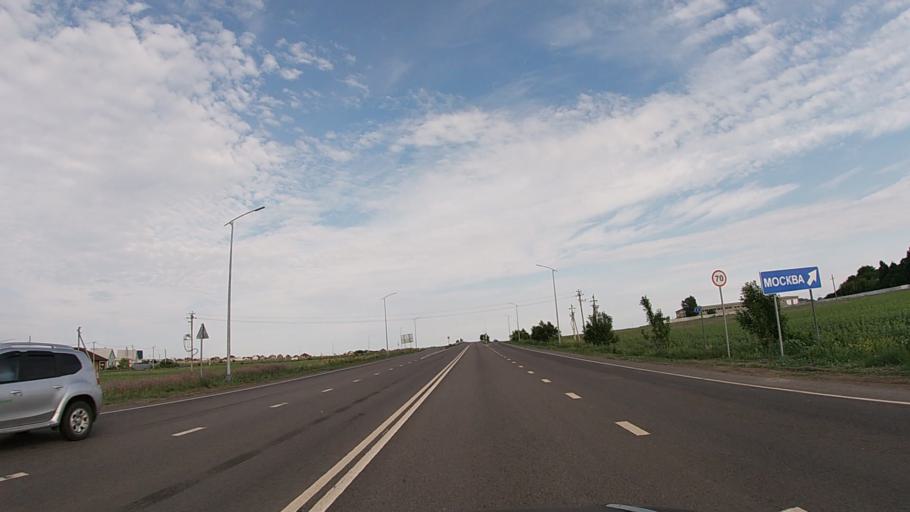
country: RU
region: Belgorod
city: Severnyy
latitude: 50.6726
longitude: 36.4791
